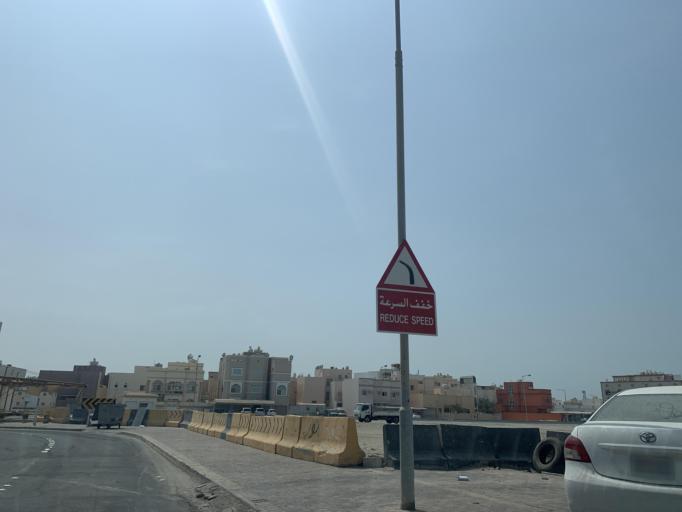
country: BH
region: Muharraq
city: Al Hadd
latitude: 26.2695
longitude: 50.6581
